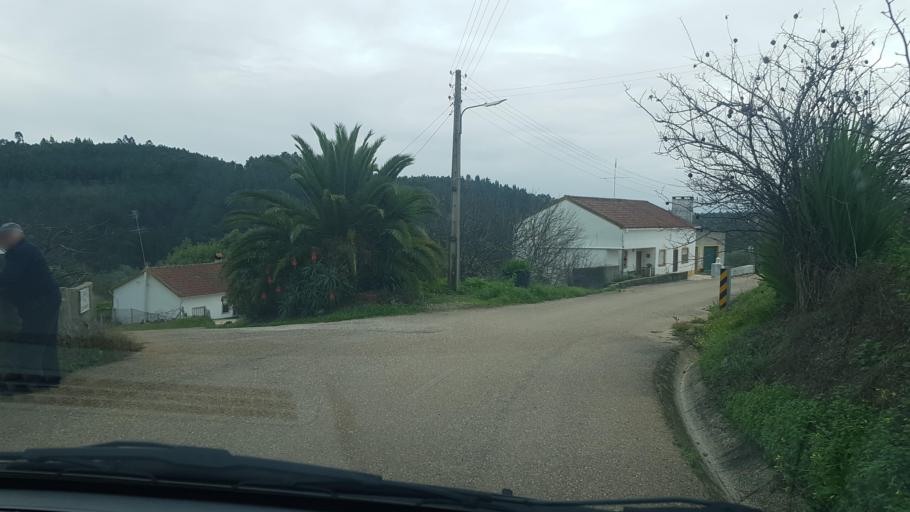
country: PT
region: Castelo Branco
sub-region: Vila de Rei
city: Vila de Rei
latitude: 39.6009
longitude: -8.1237
